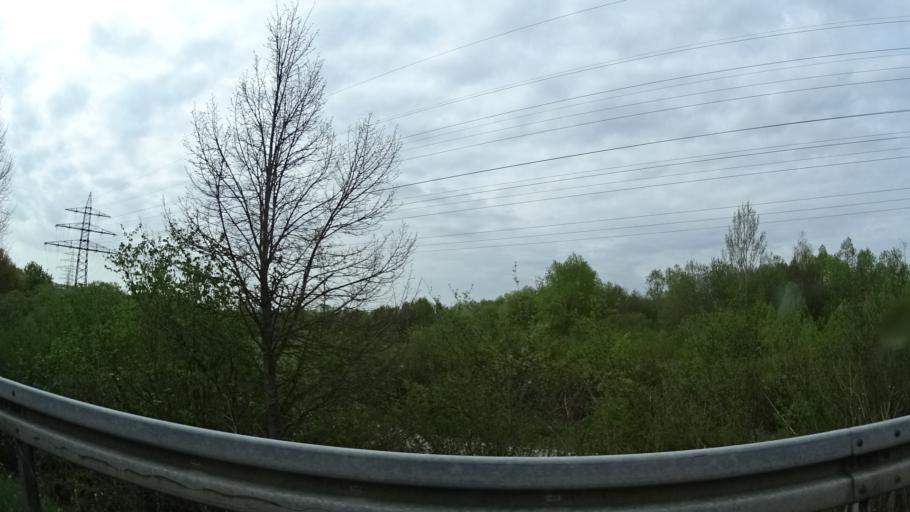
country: DE
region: Baden-Wuerttemberg
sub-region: Freiburg Region
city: Monchweiler
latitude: 48.0791
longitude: 8.4562
